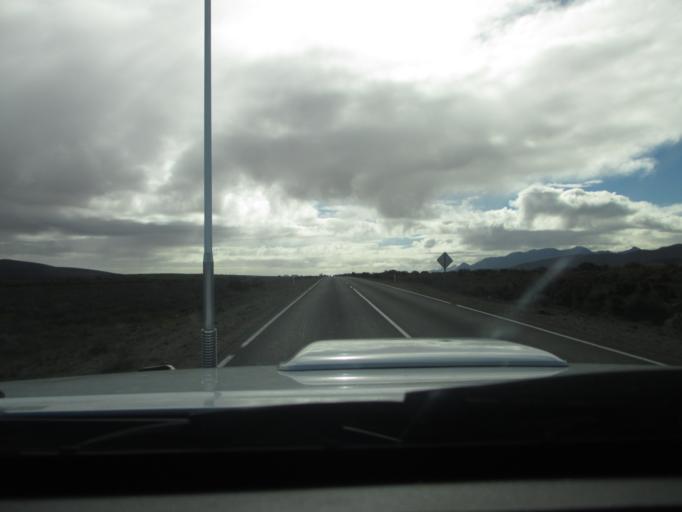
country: AU
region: South Australia
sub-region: Flinders Ranges
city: Quorn
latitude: -31.6461
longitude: 138.3818
